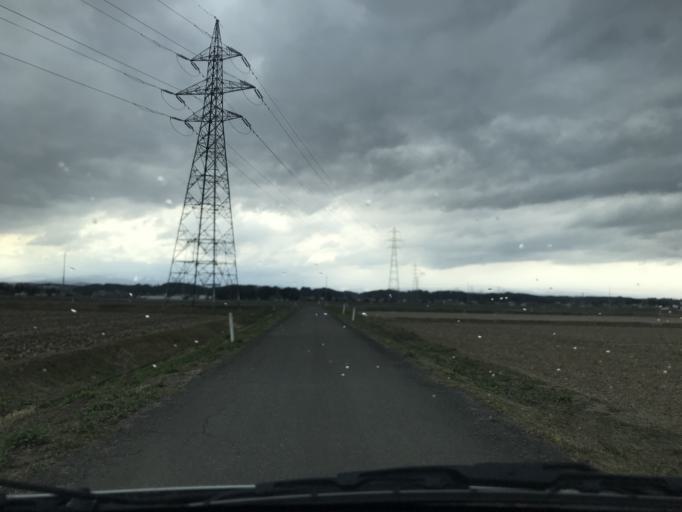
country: JP
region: Iwate
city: Mizusawa
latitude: 39.0779
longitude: 141.1619
